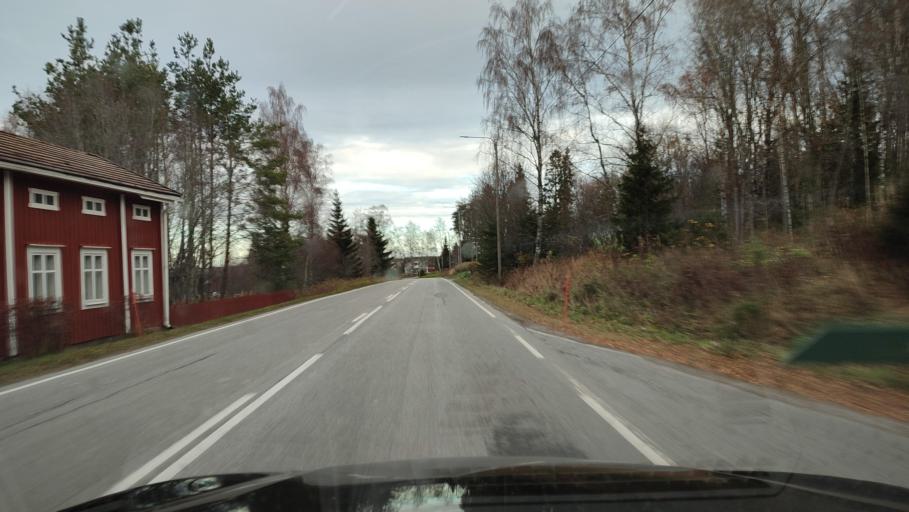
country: FI
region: Ostrobothnia
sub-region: Sydosterbotten
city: Naerpes
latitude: 62.4292
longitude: 21.3465
